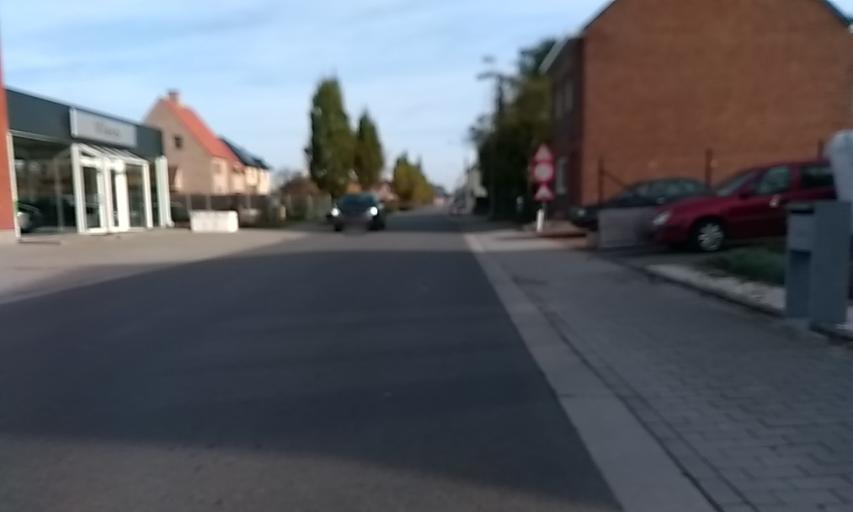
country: BE
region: Flanders
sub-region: Provincie Oost-Vlaanderen
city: Sint-Lievens-Houtem
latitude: 50.9284
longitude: 3.8913
